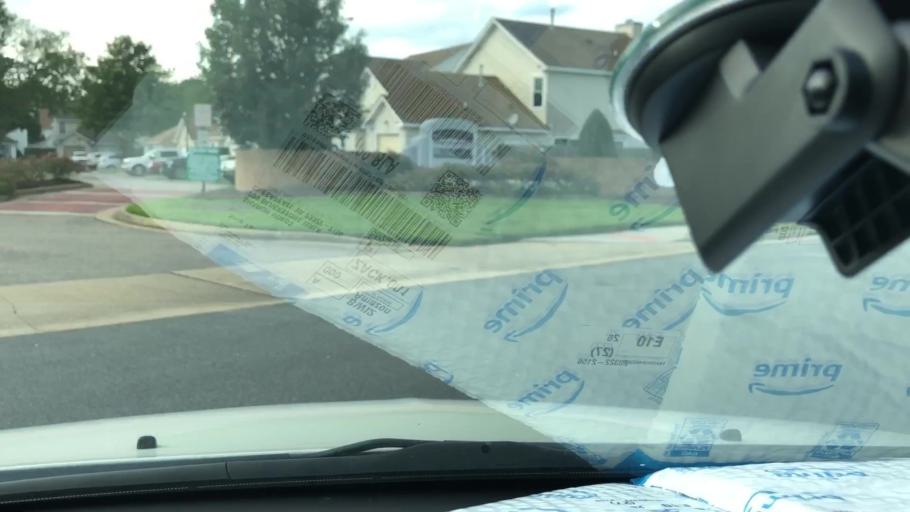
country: US
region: Virginia
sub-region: City of Chesapeake
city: Chesapeake
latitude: 36.7126
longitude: -76.2767
